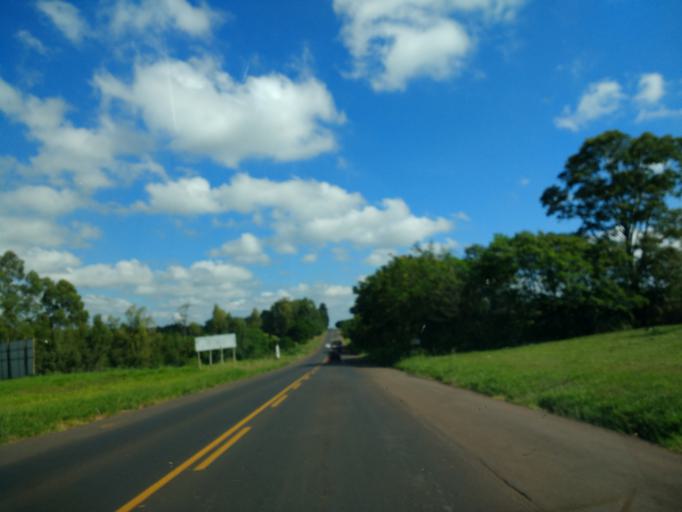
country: BR
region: Parana
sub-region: Umuarama
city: Umuarama
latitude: -23.8347
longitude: -53.3570
